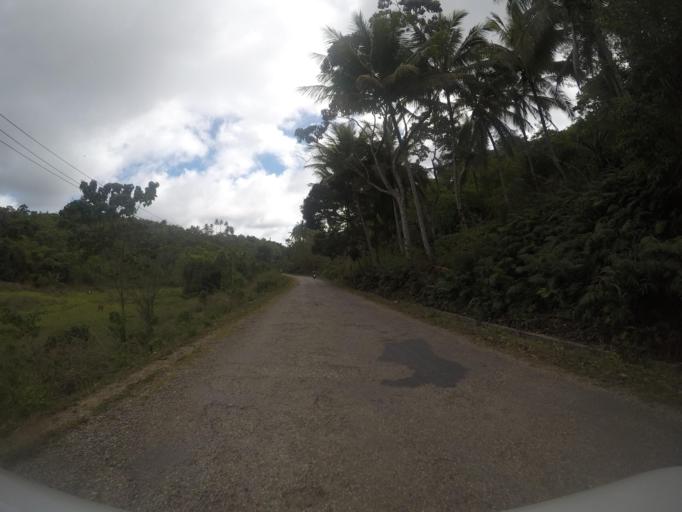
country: TL
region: Lautem
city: Lospalos
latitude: -8.5408
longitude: 126.9535
